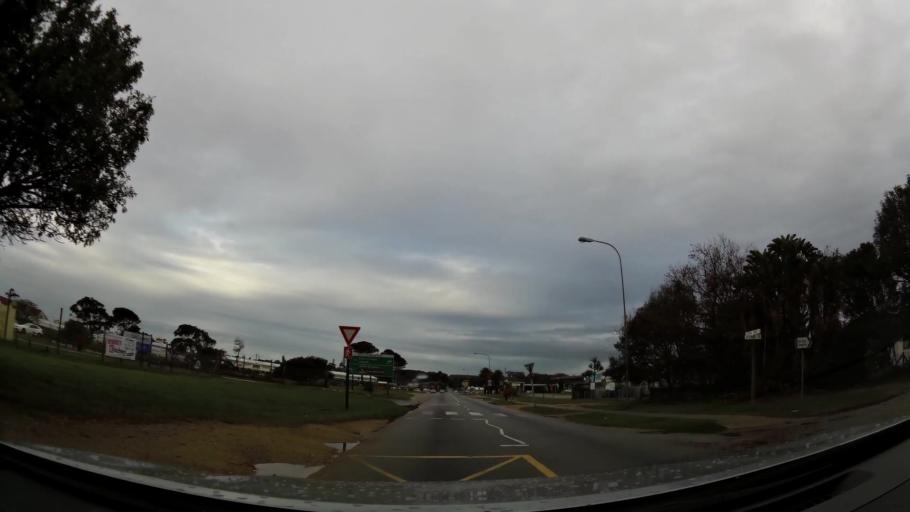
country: ZA
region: Eastern Cape
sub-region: Nelson Mandela Bay Metropolitan Municipality
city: Port Elizabeth
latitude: -33.9896
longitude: 25.5523
